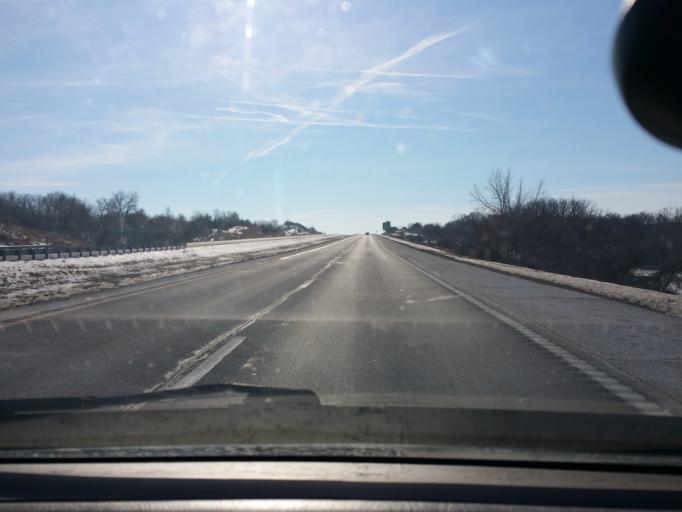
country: US
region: Missouri
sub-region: Harrison County
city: Bethany
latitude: 40.2318
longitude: -94.0131
